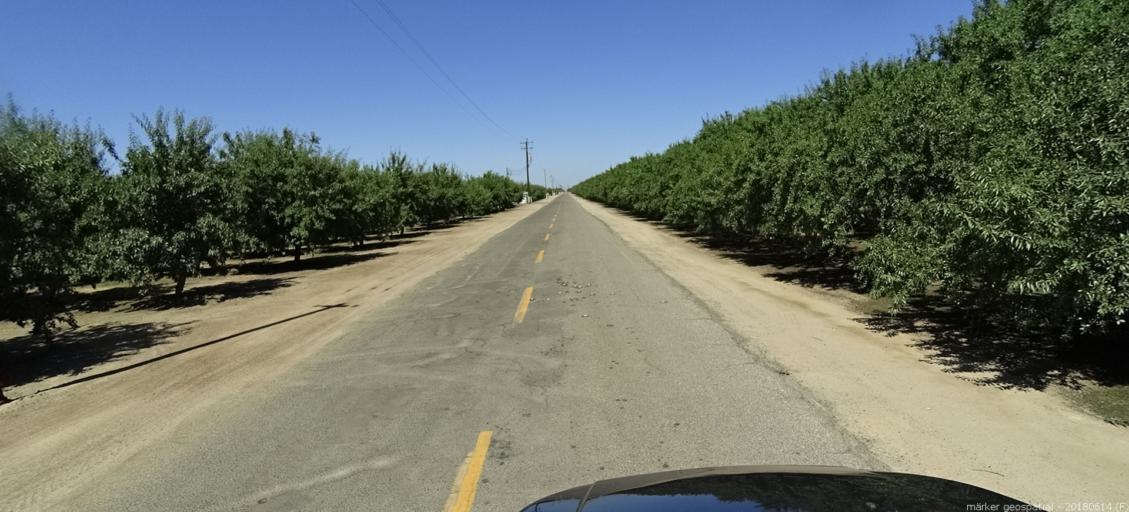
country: US
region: California
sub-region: Madera County
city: Fairmead
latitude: 36.9892
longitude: -120.1692
